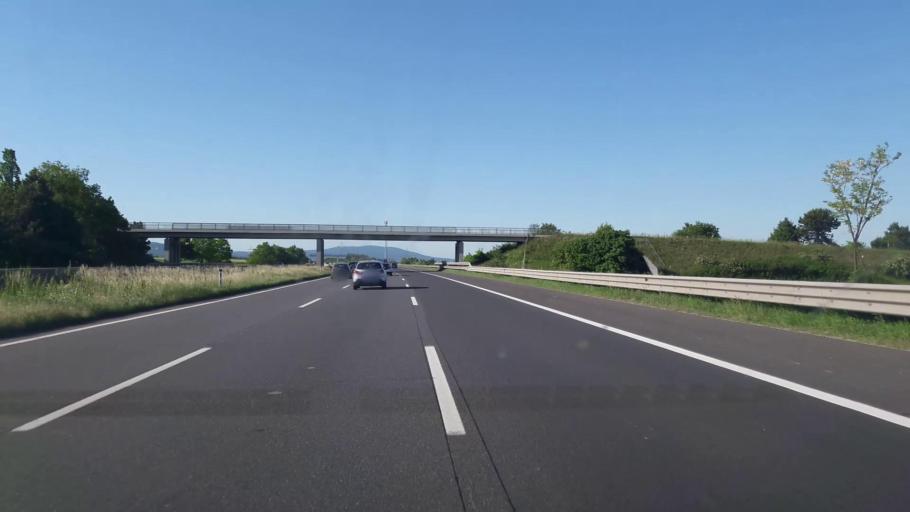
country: AT
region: Lower Austria
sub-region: Politischer Bezirk Wiener Neustadt
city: Felixdorf
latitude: 47.8854
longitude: 16.2059
